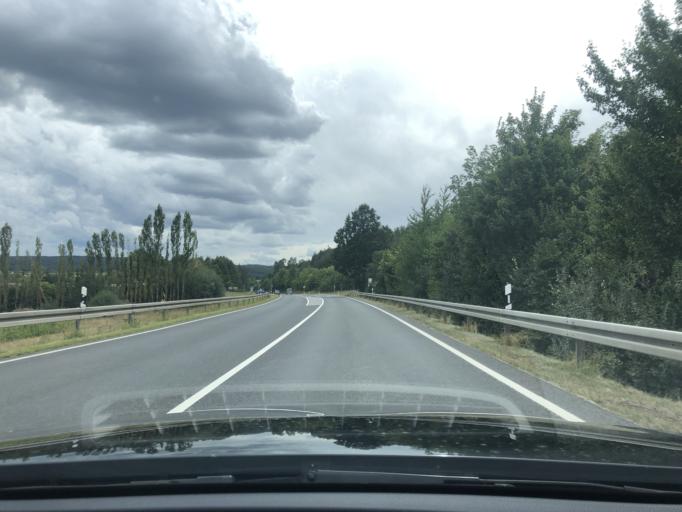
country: DE
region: Bavaria
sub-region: Regierungsbezirk Unterfranken
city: Burgpreppach
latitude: 50.1423
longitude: 10.6391
